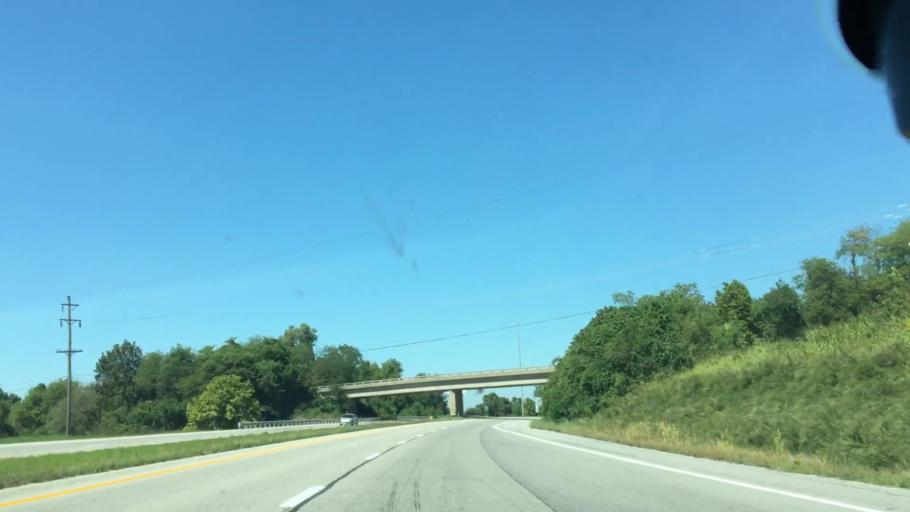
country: US
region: Kentucky
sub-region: Henderson County
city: Henderson
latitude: 37.8038
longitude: -87.5628
